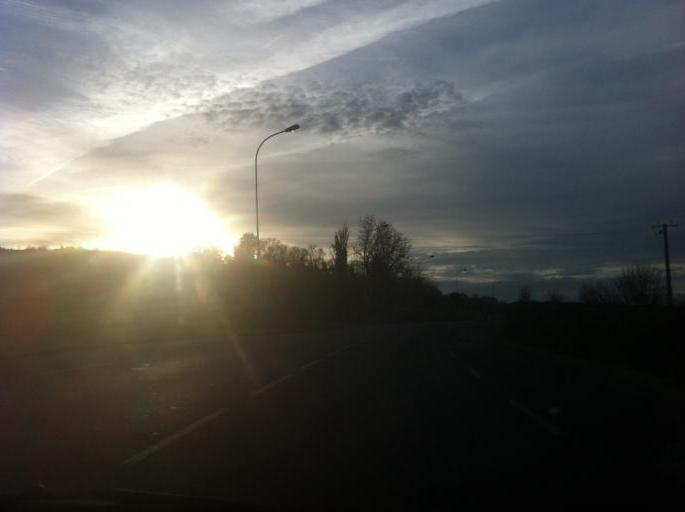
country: FR
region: Aquitaine
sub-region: Departement de la Dordogne
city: Tocane-Saint-Apre
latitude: 45.2476
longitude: 0.4679
